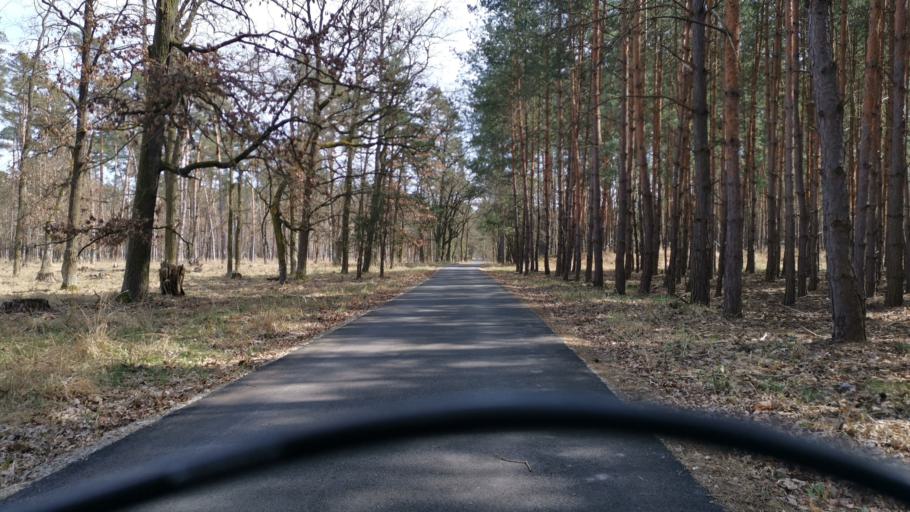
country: SK
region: Trnavsky
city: Gbely
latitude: 48.7136
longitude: 17.0582
